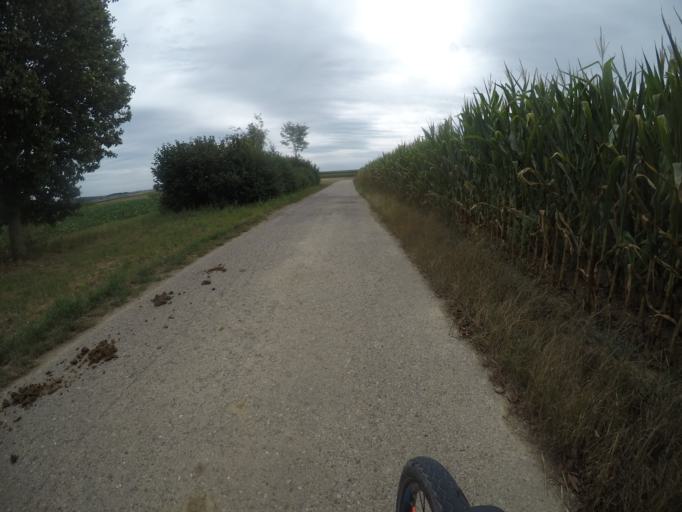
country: DE
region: Baden-Wuerttemberg
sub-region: Regierungsbezirk Stuttgart
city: Sersheim
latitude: 48.9431
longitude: 9.0020
